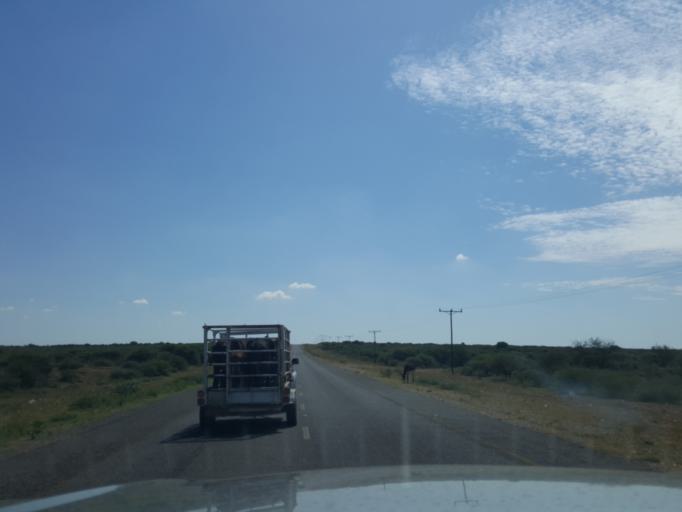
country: BW
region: Kweneng
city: Letlhakeng
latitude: -24.1184
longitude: 25.0561
